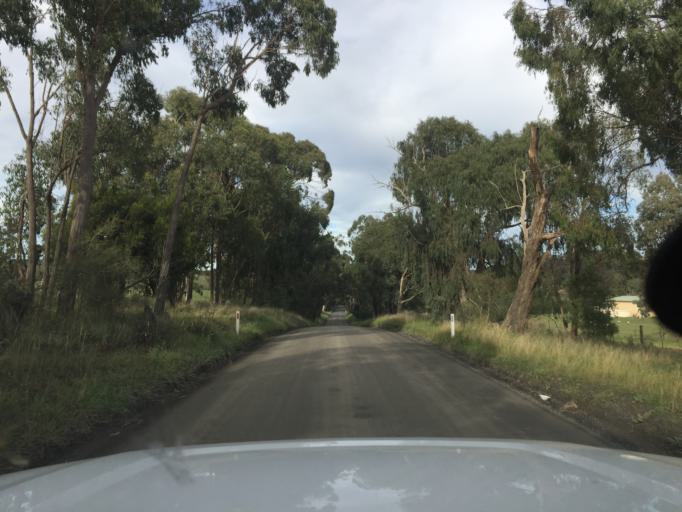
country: AU
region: Victoria
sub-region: Yarra Ranges
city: Healesville
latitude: -37.6476
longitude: 145.4707
